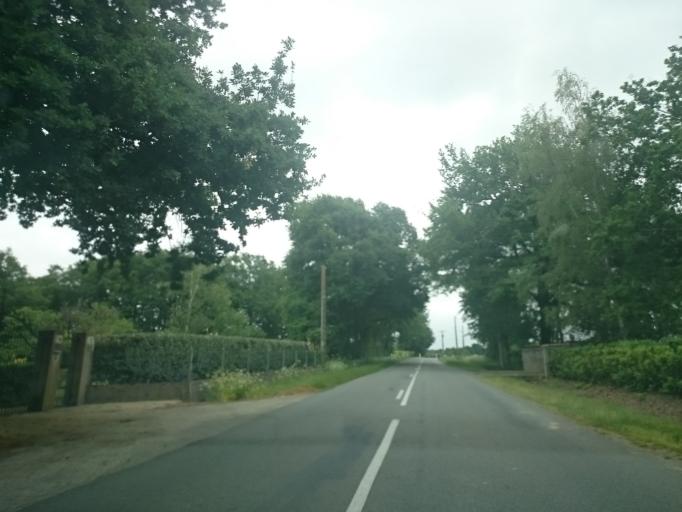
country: FR
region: Pays de la Loire
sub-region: Departement de la Loire-Atlantique
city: La Montagne
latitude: 47.1687
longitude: -1.6747
